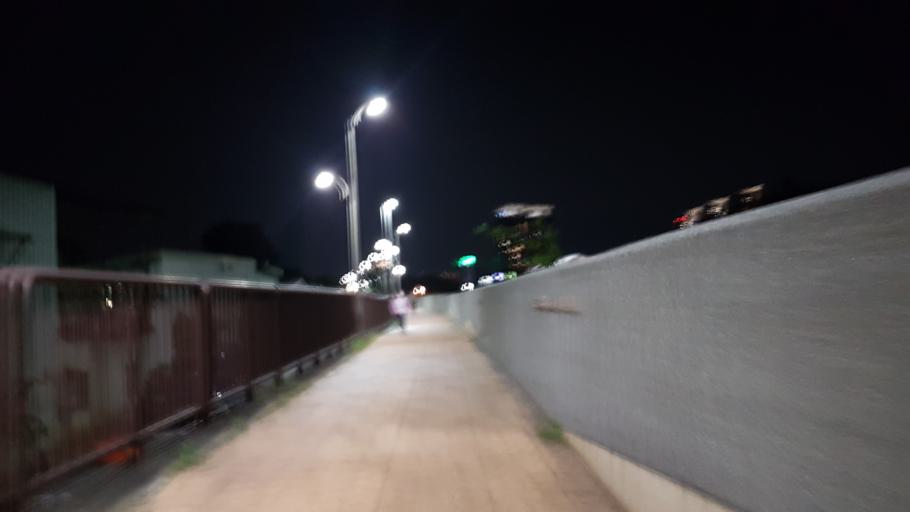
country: TW
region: Taipei
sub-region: Taipei
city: Banqiao
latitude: 24.9631
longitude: 121.5337
